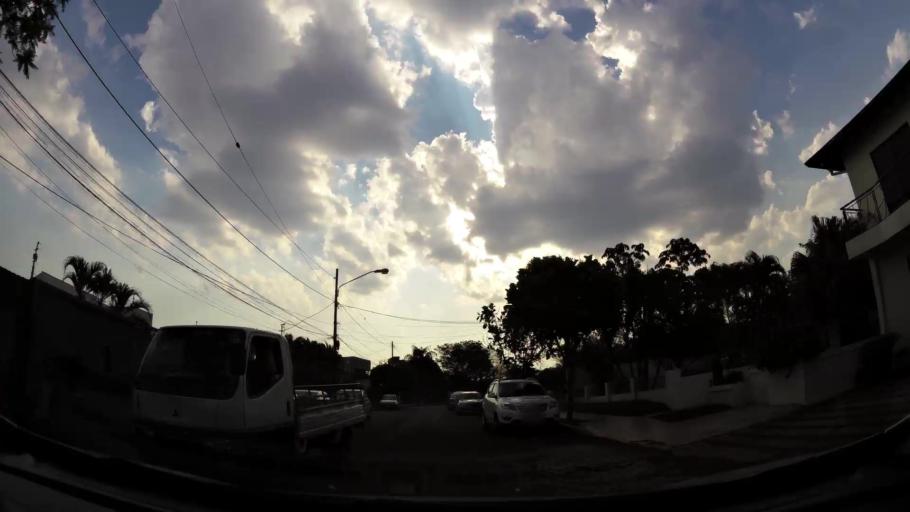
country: PY
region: Alto Parana
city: Presidente Franco
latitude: -25.5205
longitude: -54.6345
